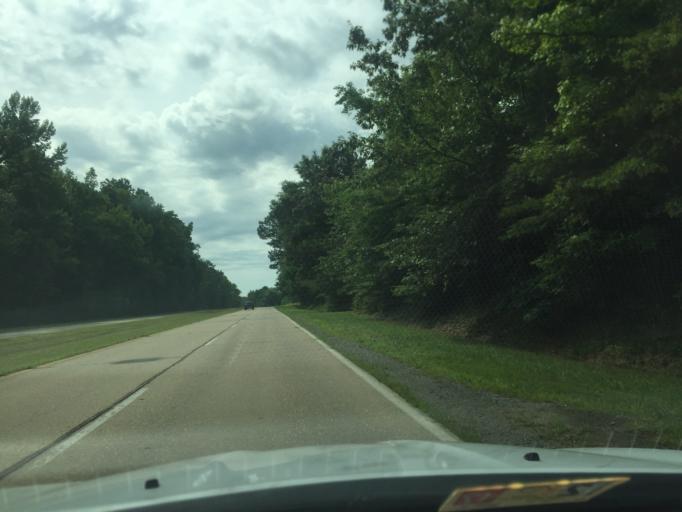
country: US
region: Virginia
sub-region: Charles City County
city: Charles City
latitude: 37.4635
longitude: -77.1043
